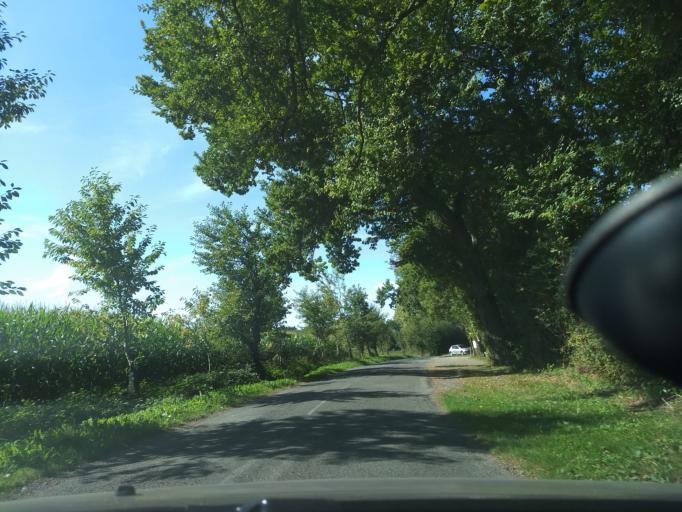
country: FR
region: Aquitaine
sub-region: Departement des Pyrenees-Atlantiques
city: Soumoulou
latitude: 43.2878
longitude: -0.1455
